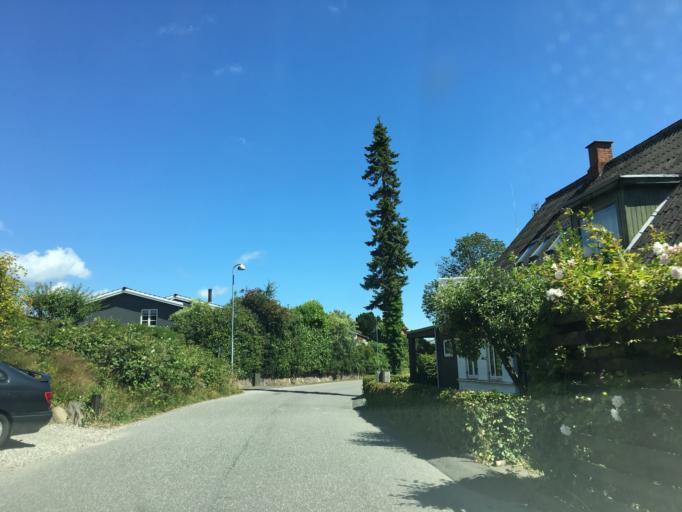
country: DK
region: South Denmark
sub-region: Svendborg Kommune
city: Thuro By
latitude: 55.0477
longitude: 10.6655
